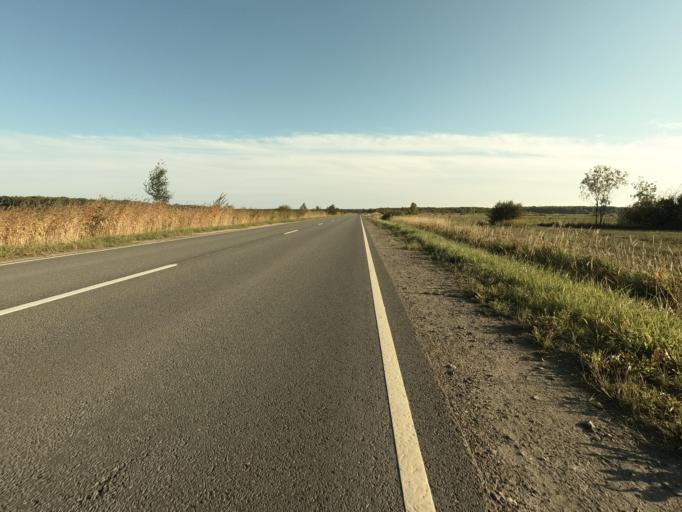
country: RU
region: St.-Petersburg
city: Sapernyy
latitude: 59.7380
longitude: 30.6533
